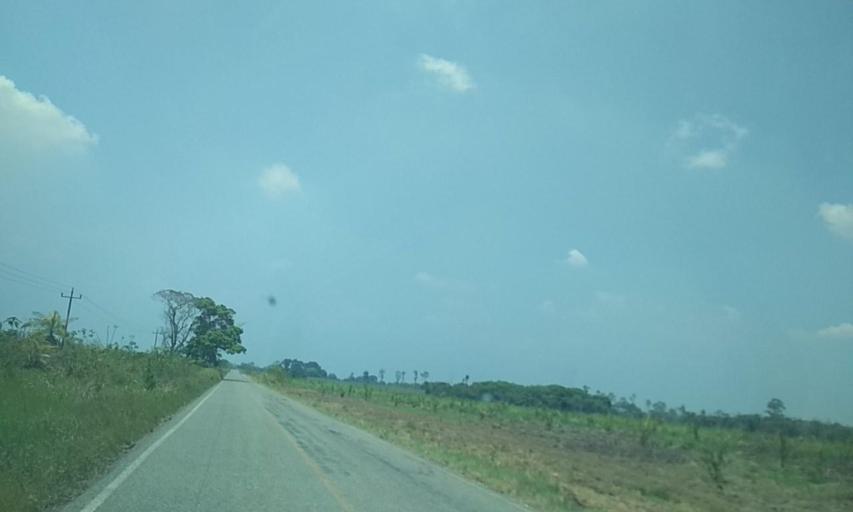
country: MX
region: Tabasco
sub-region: Huimanguillo
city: Paso de la Mina 3ra. Seccion
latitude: 17.8284
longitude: -93.6172
